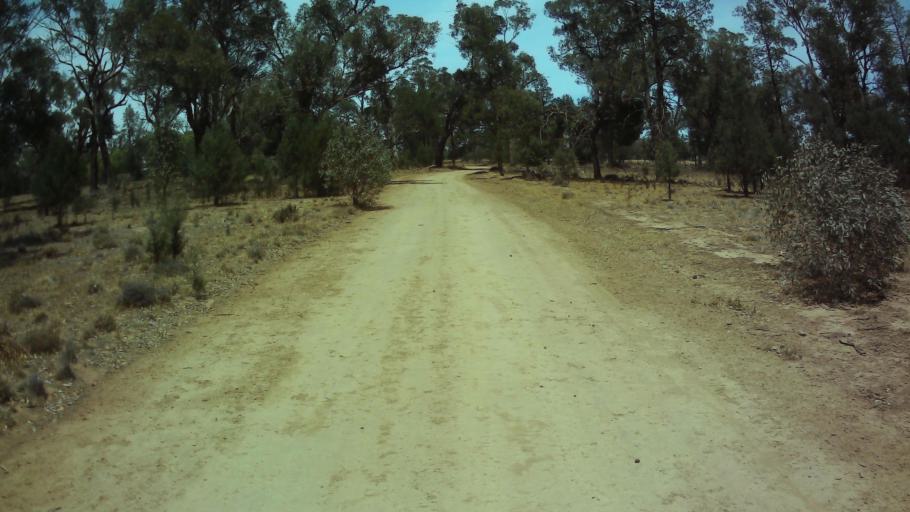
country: AU
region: New South Wales
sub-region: Weddin
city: Grenfell
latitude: -34.0350
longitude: 147.9258
